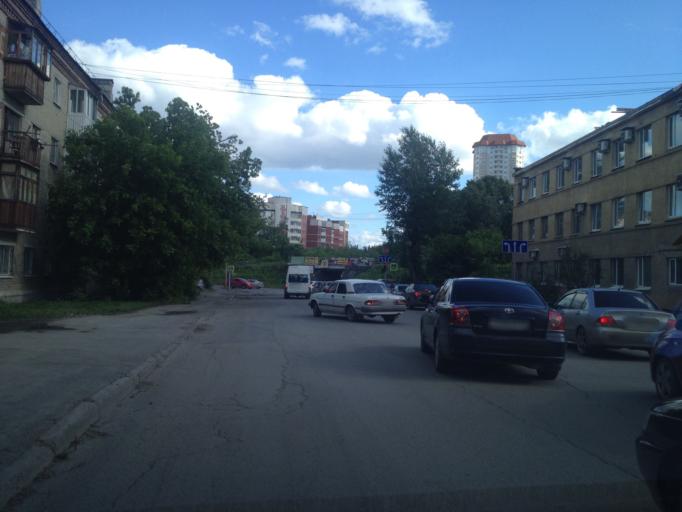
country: RU
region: Sverdlovsk
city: Yekaterinburg
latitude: 56.8564
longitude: 60.5818
